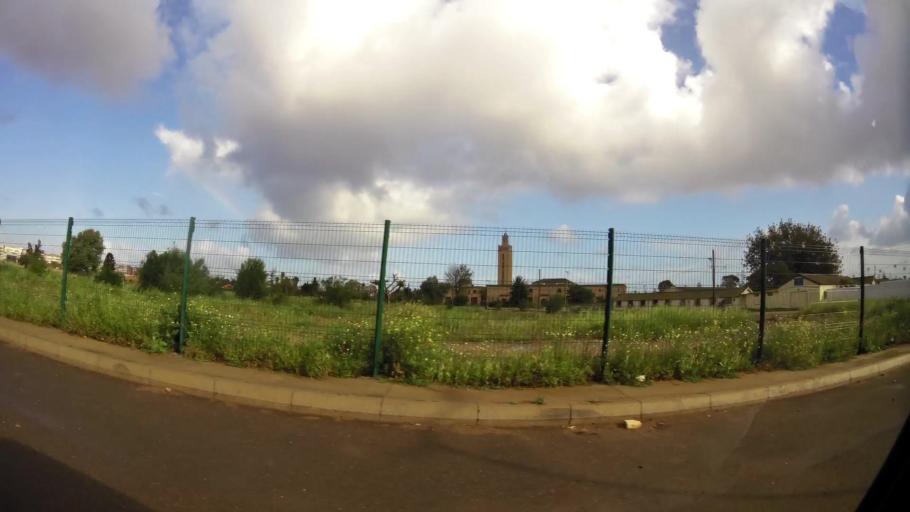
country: MA
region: Grand Casablanca
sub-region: Casablanca
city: Casablanca
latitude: 33.5665
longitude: -7.6622
